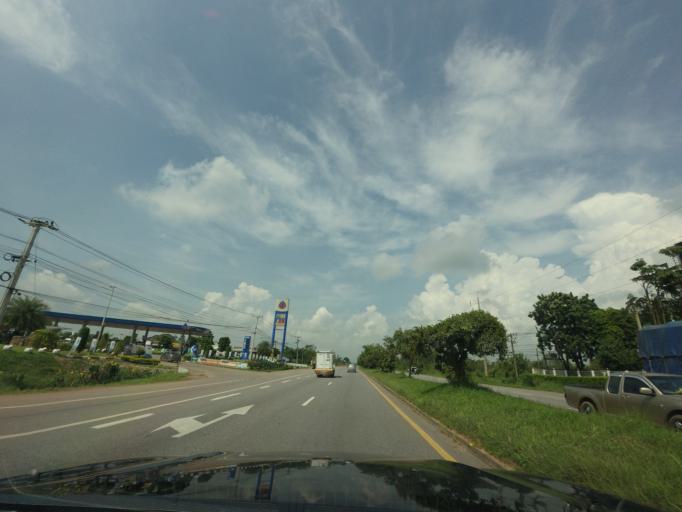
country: TH
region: Khon Kaen
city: Khon Kaen
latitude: 16.4506
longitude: 102.7392
